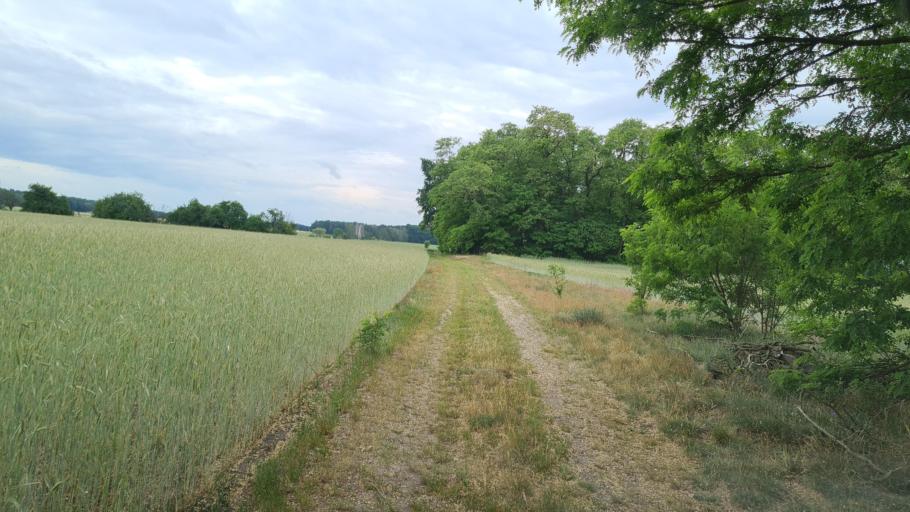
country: DE
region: Brandenburg
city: Bronkow
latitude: 51.6253
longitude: 13.9370
